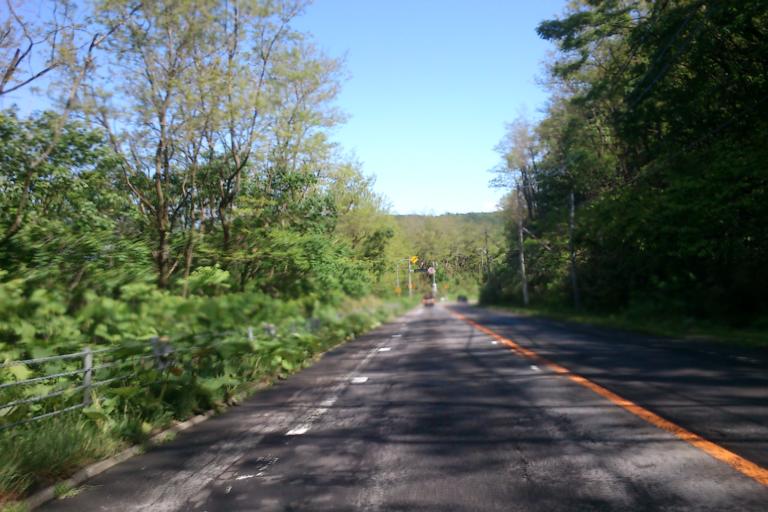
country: JP
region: Hokkaido
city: Ishikari
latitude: 43.5500
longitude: 141.3982
